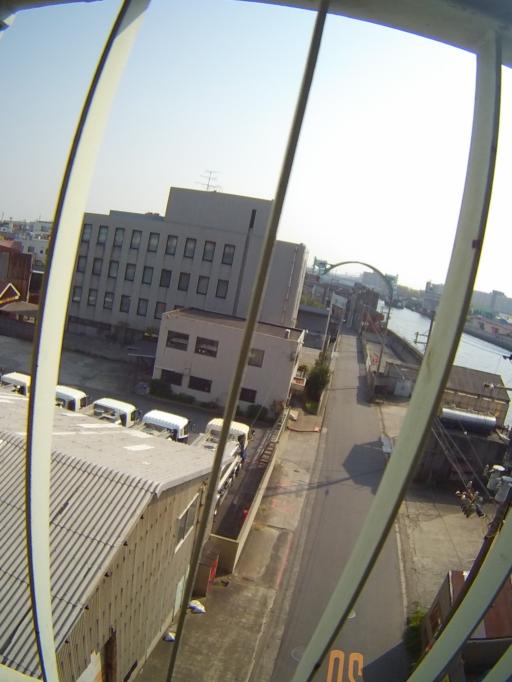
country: JP
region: Osaka
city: Osaka-shi
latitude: 34.6543
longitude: 135.4815
